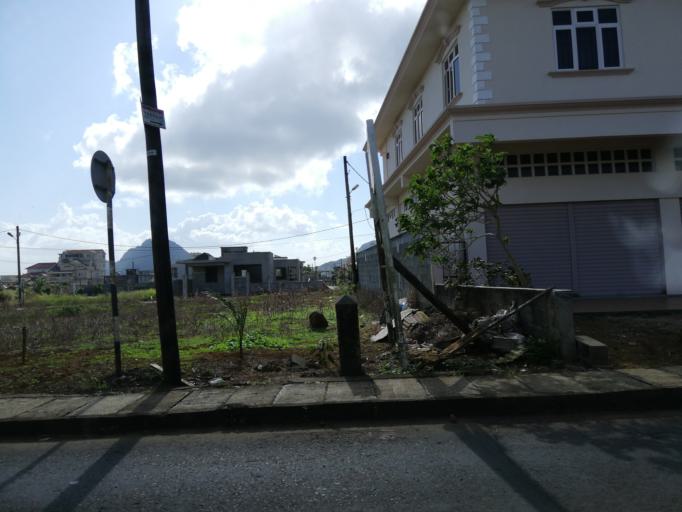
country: MU
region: Moka
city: Verdun
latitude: -20.2204
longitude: 57.5488
